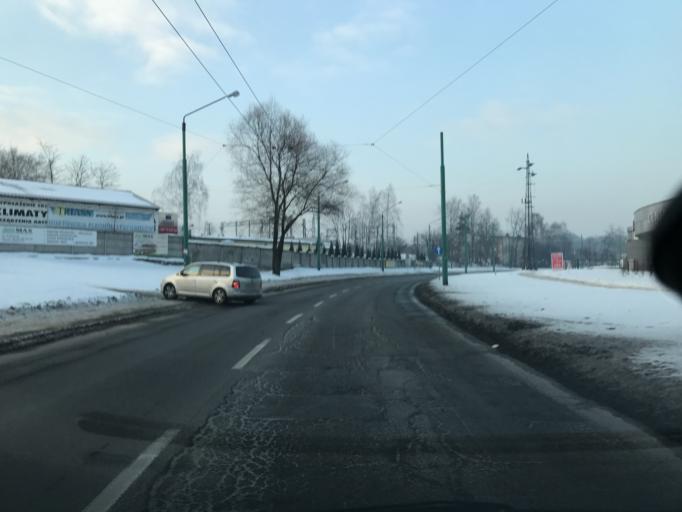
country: PL
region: Silesian Voivodeship
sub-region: Tychy
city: Tychy
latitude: 50.1301
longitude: 18.9649
